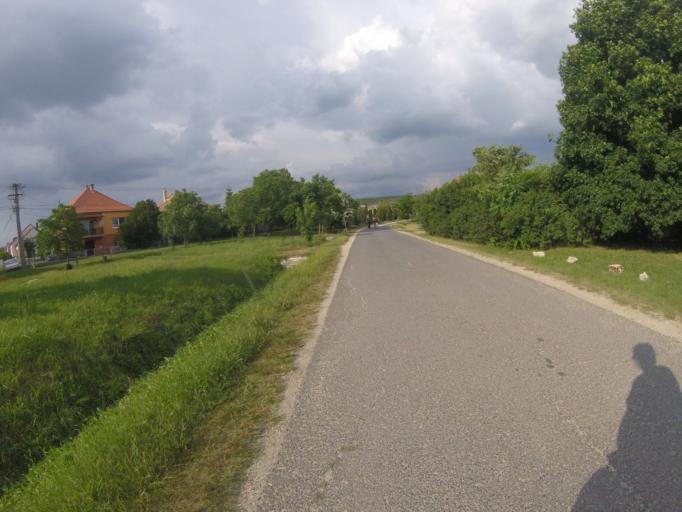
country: HU
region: Fejer
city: Szarliget
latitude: 47.4814
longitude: 18.5215
